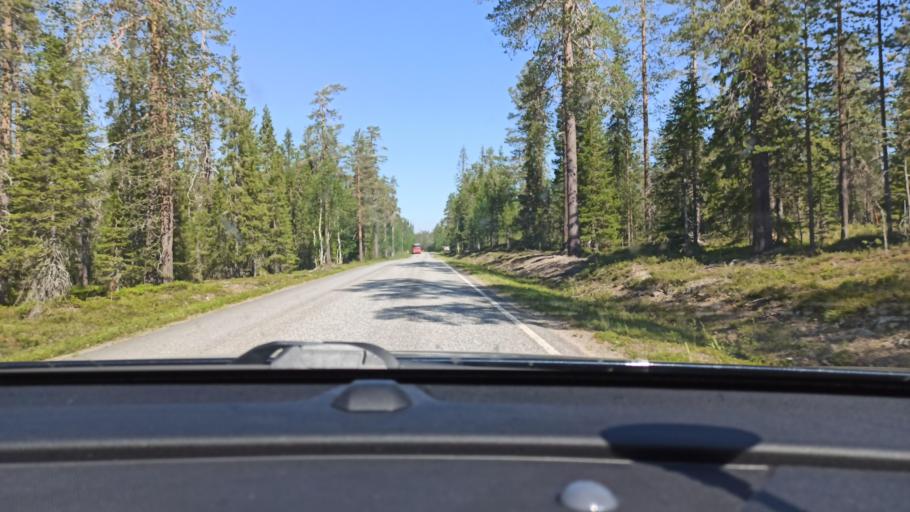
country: FI
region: Lapland
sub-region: Tunturi-Lappi
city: Kolari
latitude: 67.6635
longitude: 24.1629
